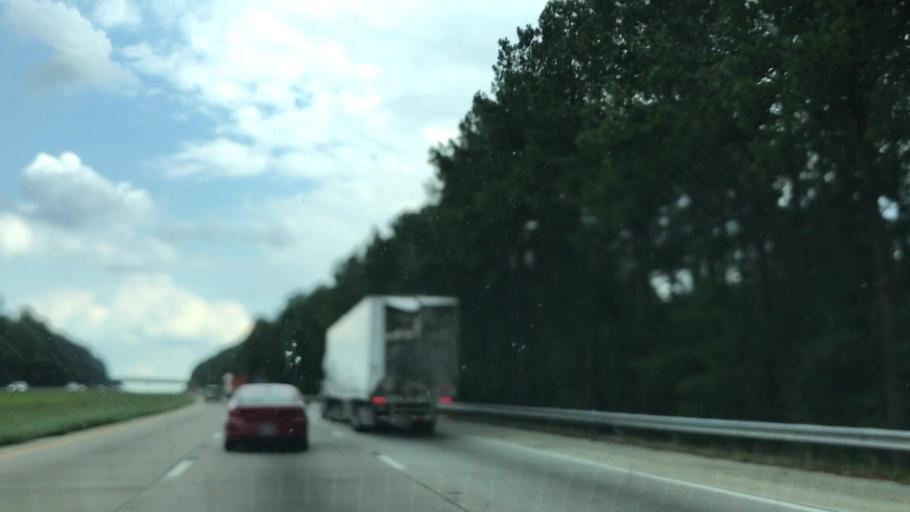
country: US
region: South Carolina
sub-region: Fairfield County
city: Winnsboro Mills
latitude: 34.3189
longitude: -81.0057
